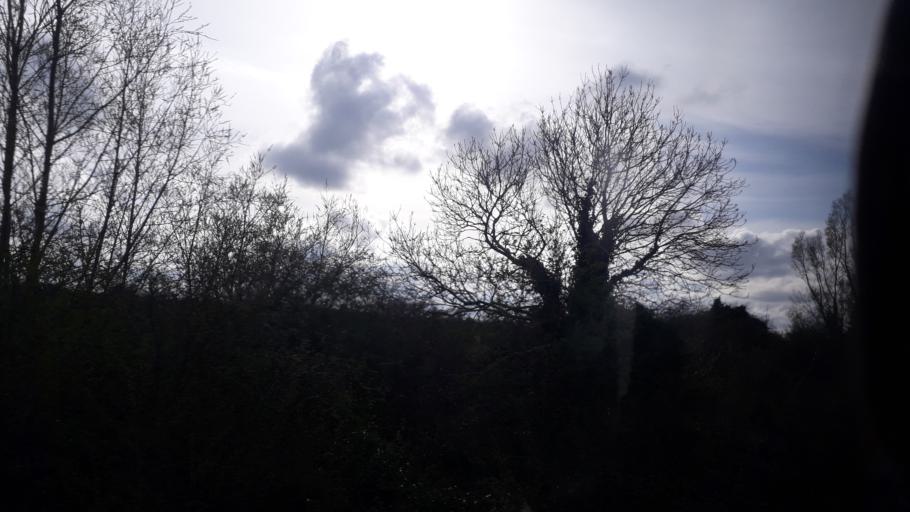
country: IE
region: Leinster
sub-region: An Mhi
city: Longwood
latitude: 53.4452
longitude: -6.9419
